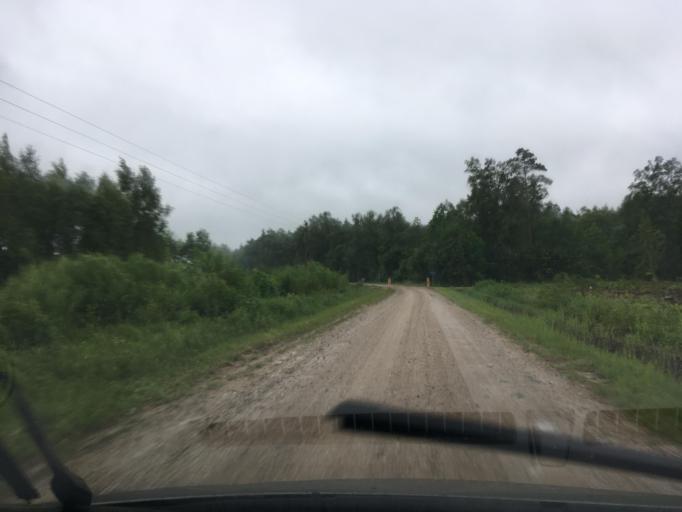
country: EE
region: Laeaene
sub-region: Lihula vald
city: Lihula
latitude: 58.6099
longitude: 23.8272
